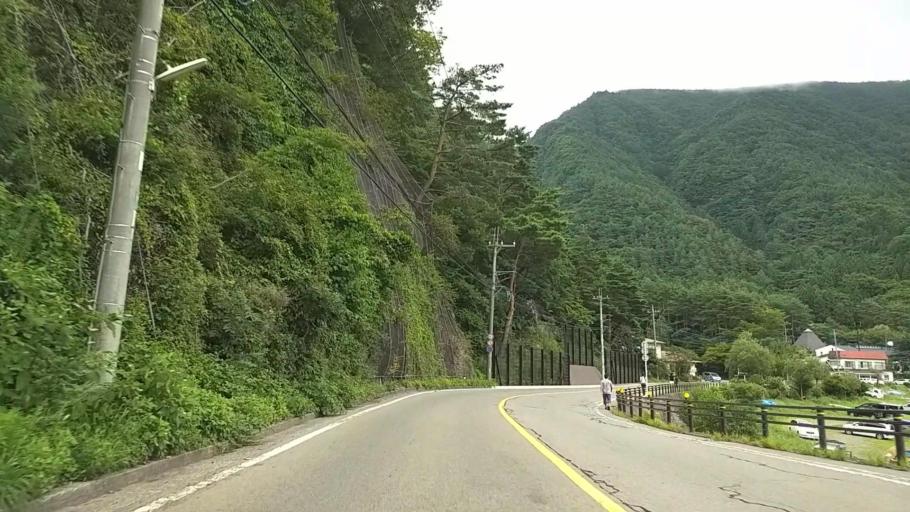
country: JP
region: Yamanashi
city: Fujikawaguchiko
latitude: 35.5016
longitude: 138.6984
